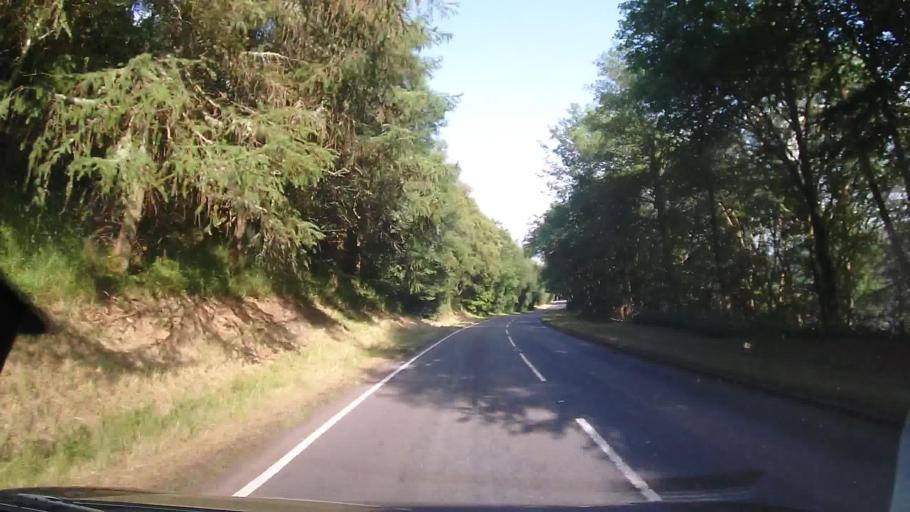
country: GB
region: Wales
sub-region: Gwynedd
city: Bala
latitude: 52.9544
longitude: -3.6942
